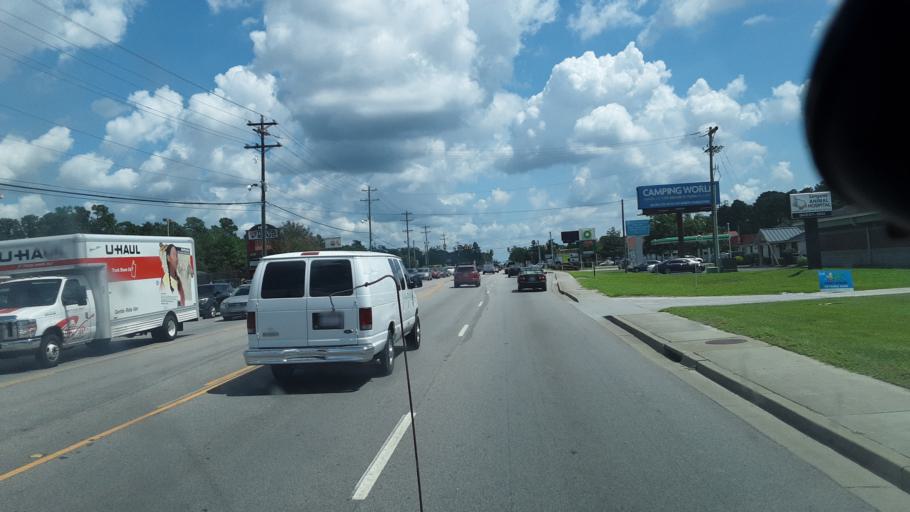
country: US
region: South Carolina
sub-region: Berkeley County
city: Sangaree
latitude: 33.0406
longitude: -80.1364
